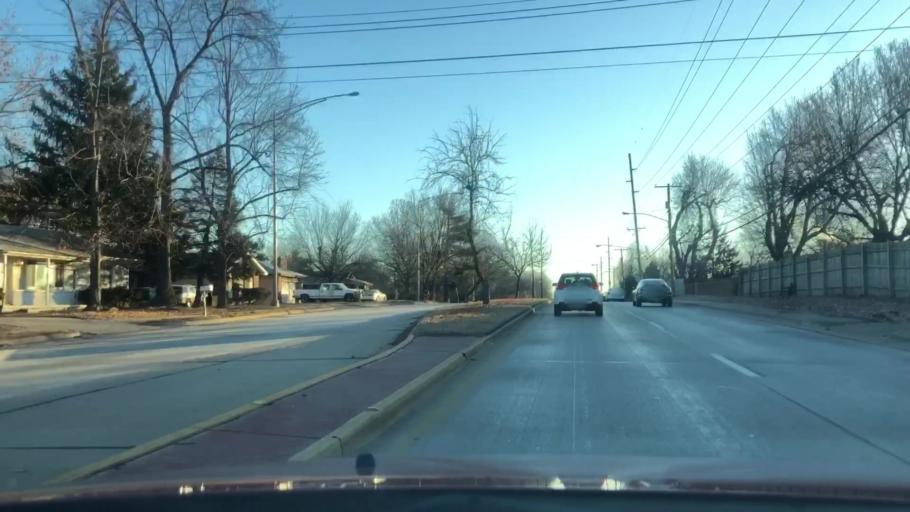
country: US
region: Missouri
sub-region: Greene County
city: Springfield
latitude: 37.1589
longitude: -93.2526
